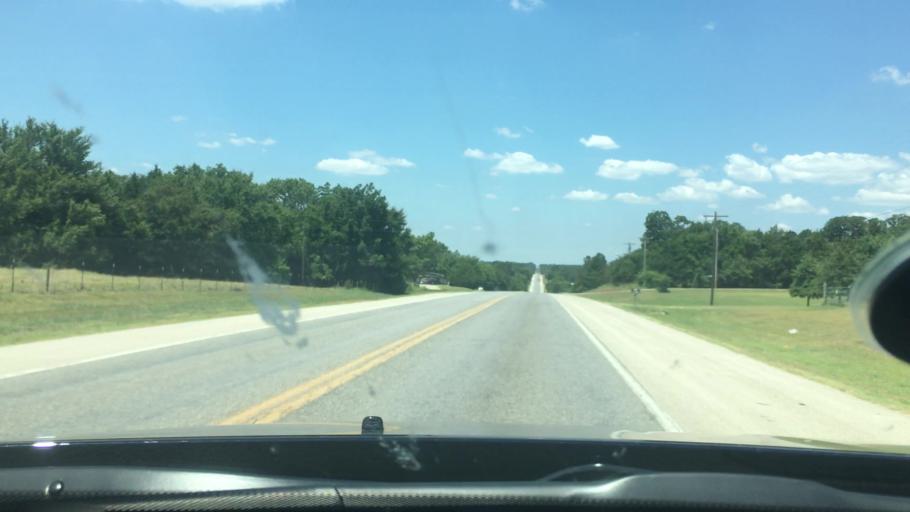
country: US
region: Oklahoma
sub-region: Carter County
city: Dickson
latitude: 34.1873
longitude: -96.9117
